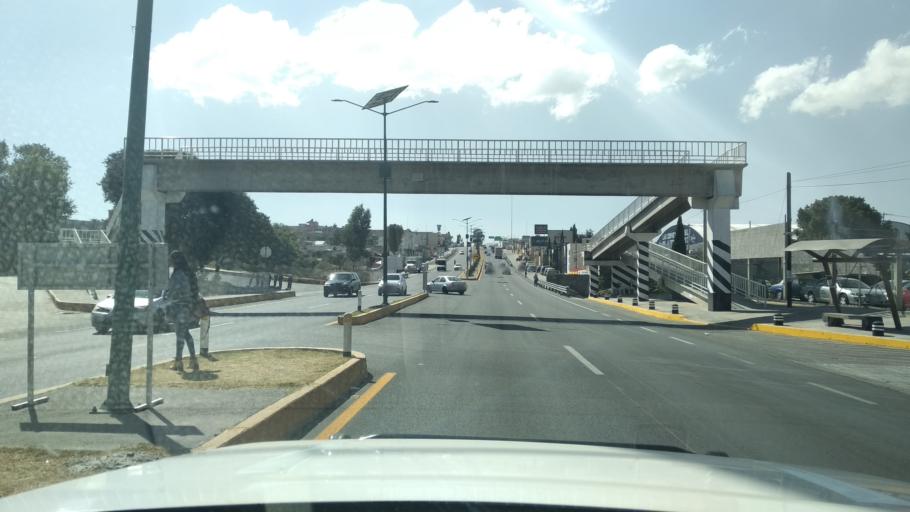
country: MX
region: Hidalgo
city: Calpulalpan
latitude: 19.5924
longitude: -98.5710
